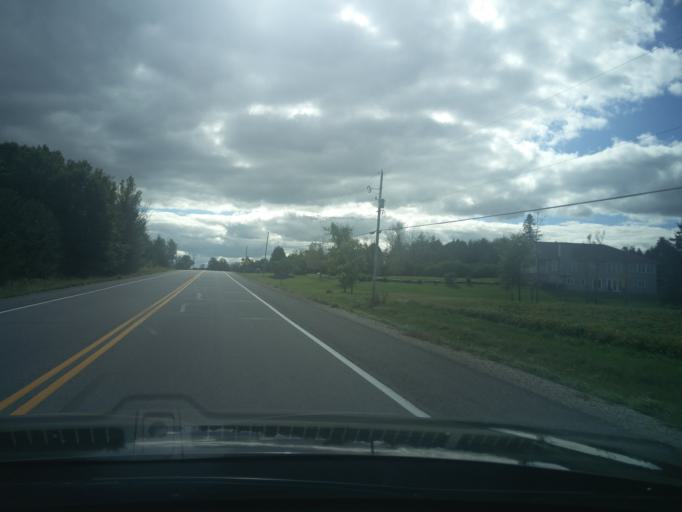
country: CA
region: Ontario
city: Perth
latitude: 44.9723
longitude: -76.1399
